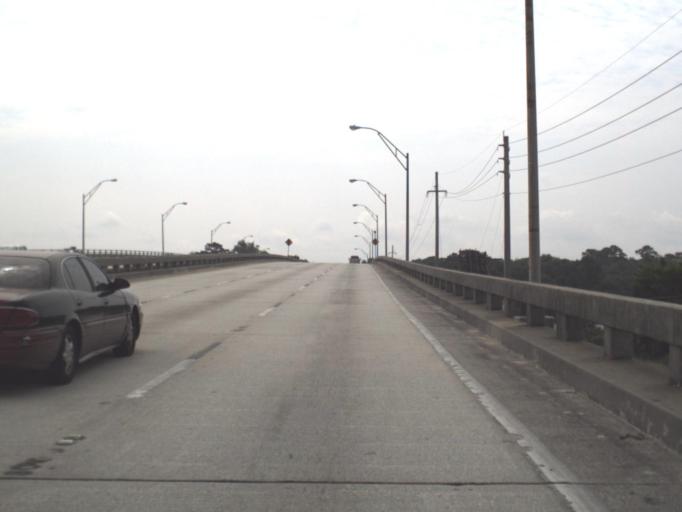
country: US
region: Florida
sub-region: Duval County
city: Jacksonville
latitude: 30.2753
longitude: -81.7186
